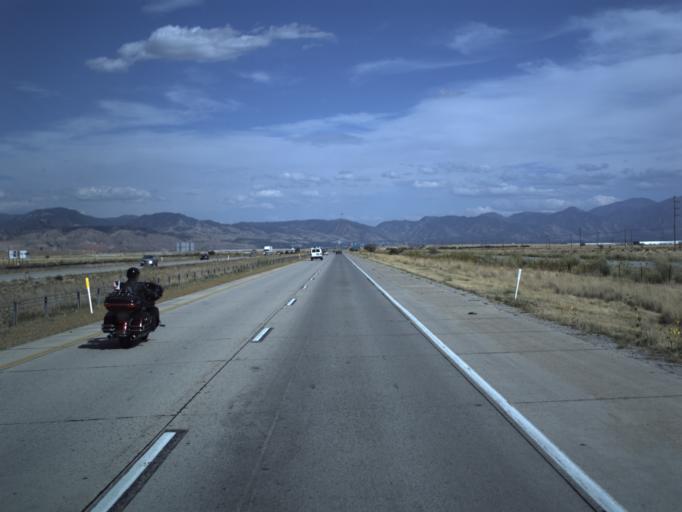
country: US
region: Utah
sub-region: Salt Lake County
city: Magna
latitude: 40.7708
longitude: -112.0869
